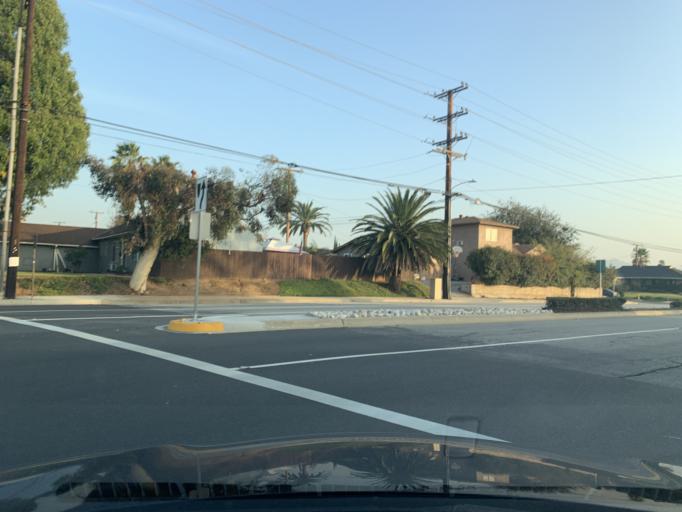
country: US
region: California
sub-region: Los Angeles County
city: Covina
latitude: 34.0913
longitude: -117.8727
